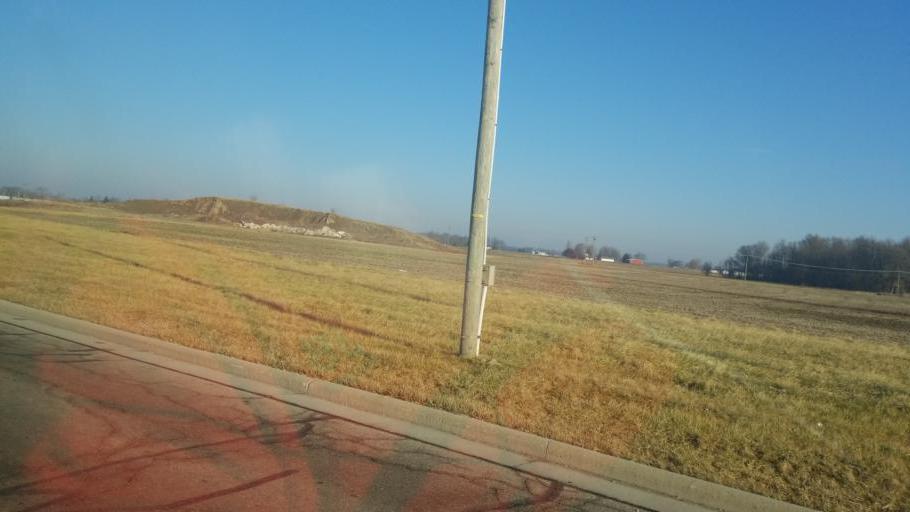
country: US
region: Ohio
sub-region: Crawford County
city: Bucyrus
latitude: 40.8315
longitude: -82.9646
